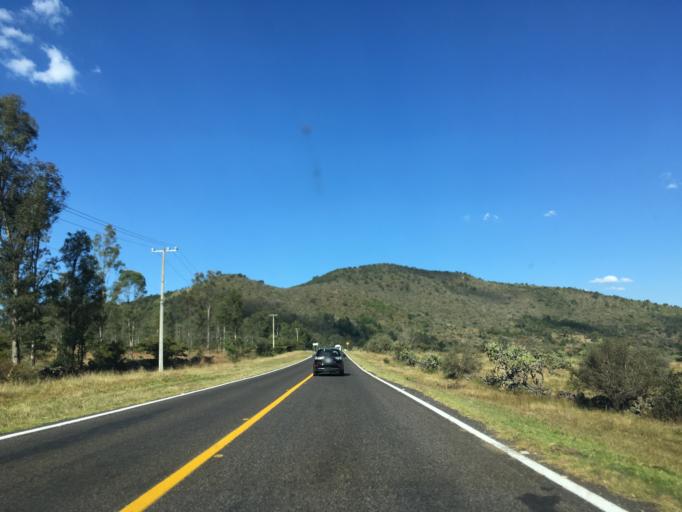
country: MX
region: Michoacan
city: Tzintzuntzan
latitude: 19.5848
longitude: -101.5780
